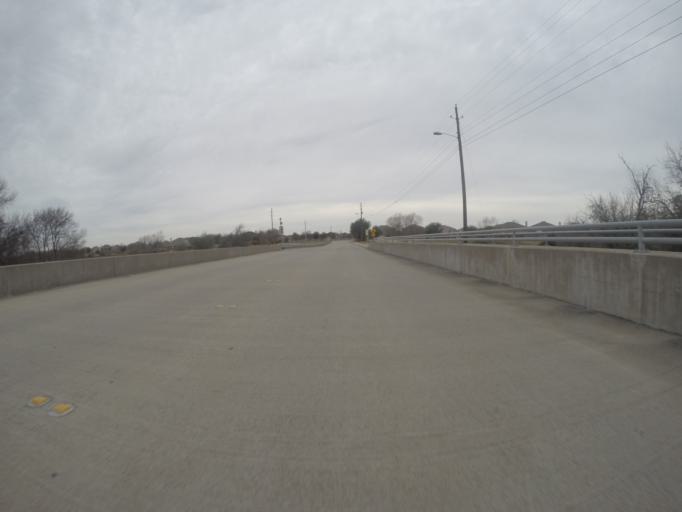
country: US
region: Texas
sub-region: Collin County
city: Saint Paul
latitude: 33.0419
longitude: -96.5658
